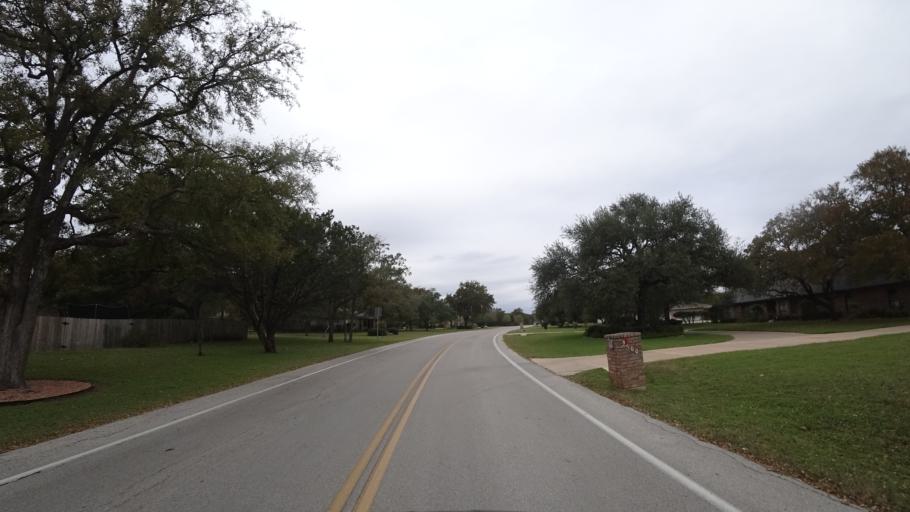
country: US
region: Texas
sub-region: Travis County
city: Shady Hollow
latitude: 30.1558
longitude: -97.8703
